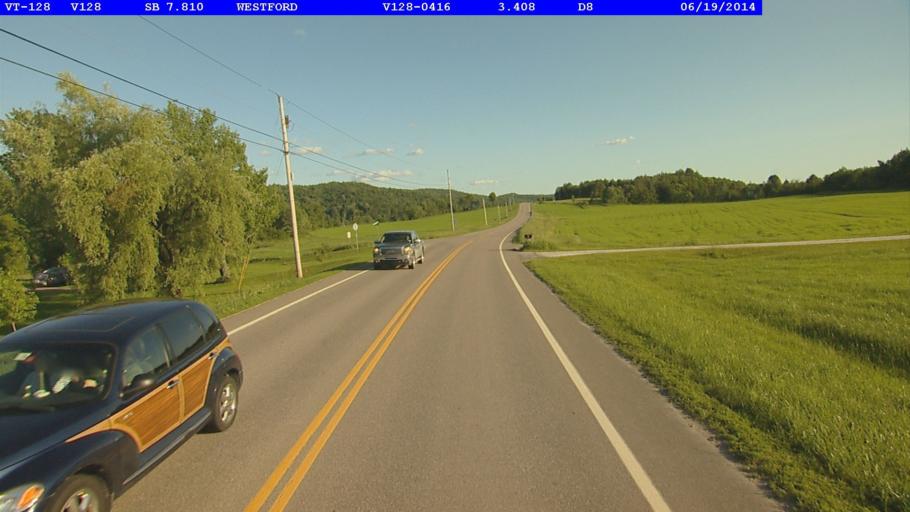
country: US
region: Vermont
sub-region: Chittenden County
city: Jericho
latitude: 44.6061
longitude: -73.0088
